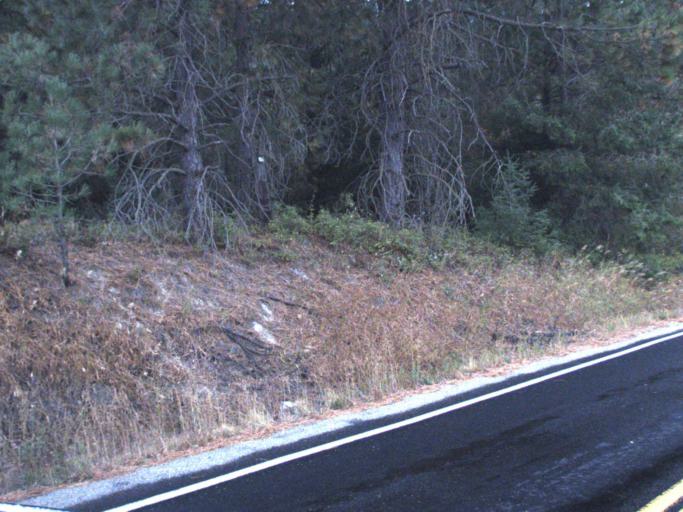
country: US
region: Washington
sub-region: Stevens County
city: Chewelah
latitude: 48.1141
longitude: -117.7554
